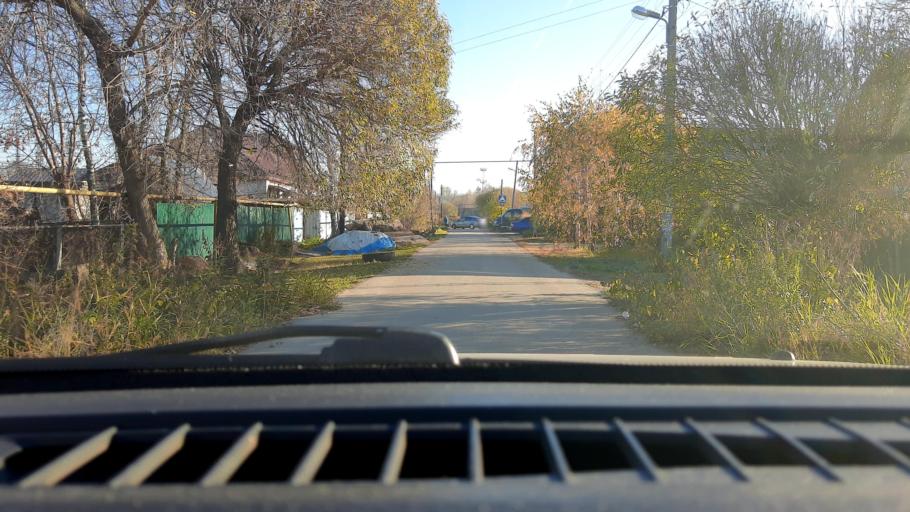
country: RU
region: Nizjnij Novgorod
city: Nizhniy Novgorod
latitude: 56.2910
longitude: 43.8989
